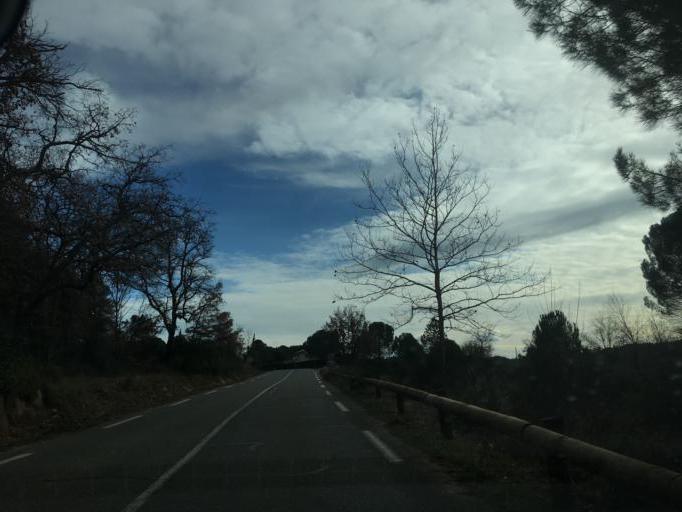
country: FR
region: Provence-Alpes-Cote d'Azur
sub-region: Departement du Var
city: Le Val
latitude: 43.4427
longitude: 6.0356
